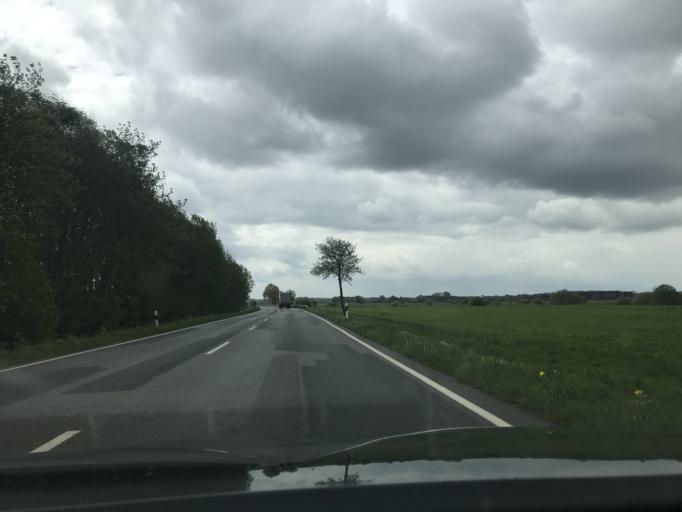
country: DE
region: Lower Saxony
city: Hude
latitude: 53.1270
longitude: 8.5364
